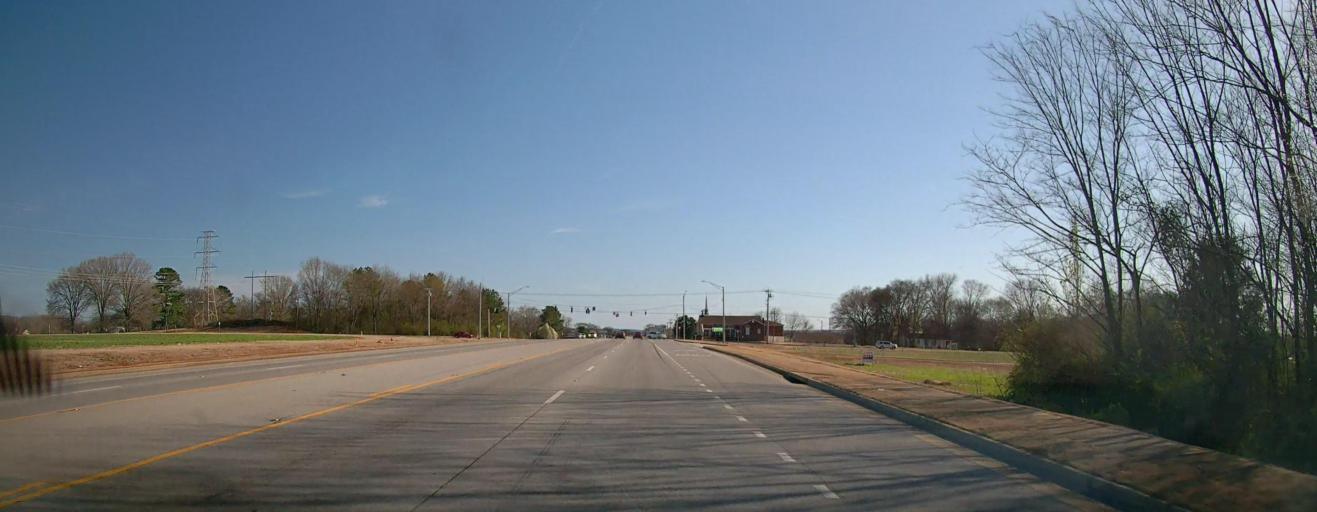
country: US
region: Alabama
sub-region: Colbert County
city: Muscle Shoals
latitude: 34.7313
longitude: -87.6352
